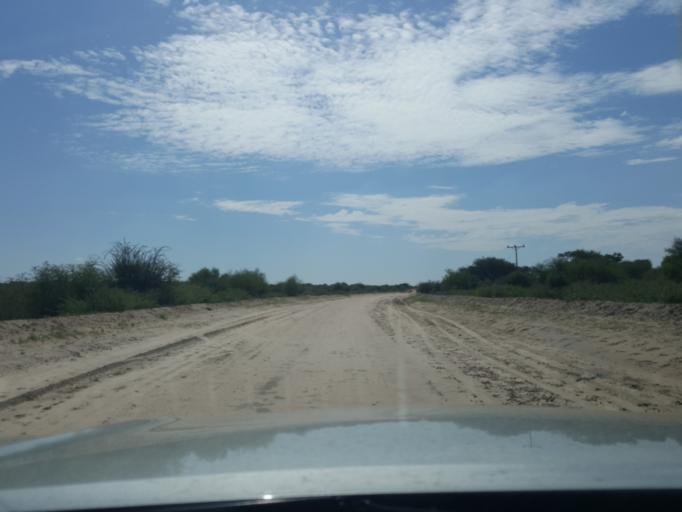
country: BW
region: Kweneng
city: Letlhakeng
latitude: -24.0520
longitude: 25.0261
